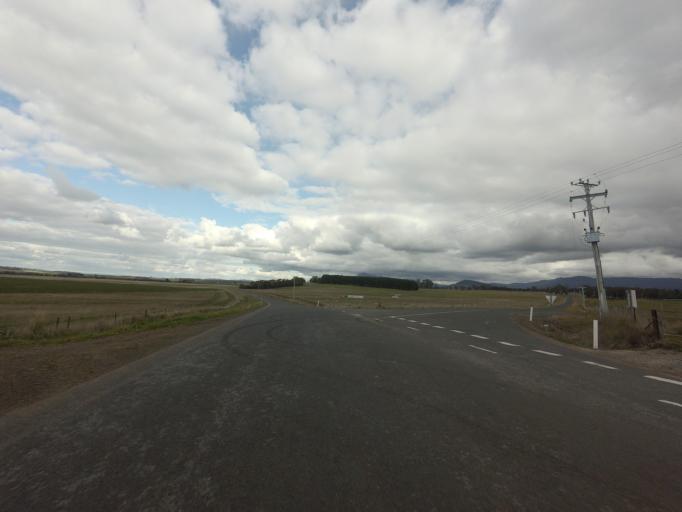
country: AU
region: Tasmania
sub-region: Northern Midlands
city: Longford
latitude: -41.7734
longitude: 147.0905
